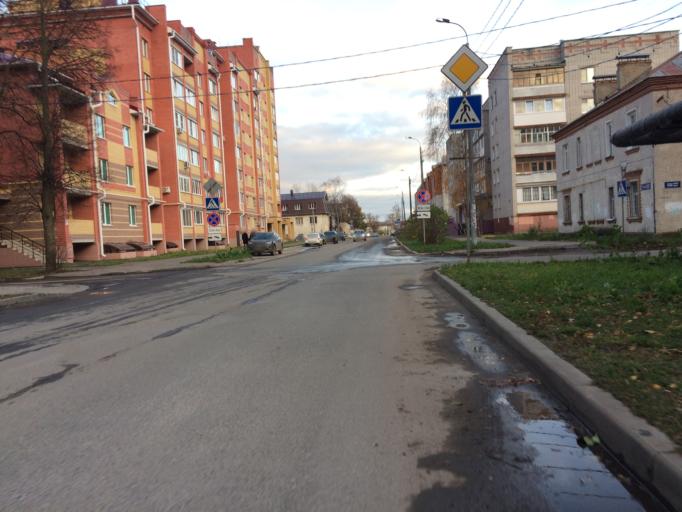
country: RU
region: Mariy-El
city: Yoshkar-Ola
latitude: 56.6475
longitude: 47.8958
